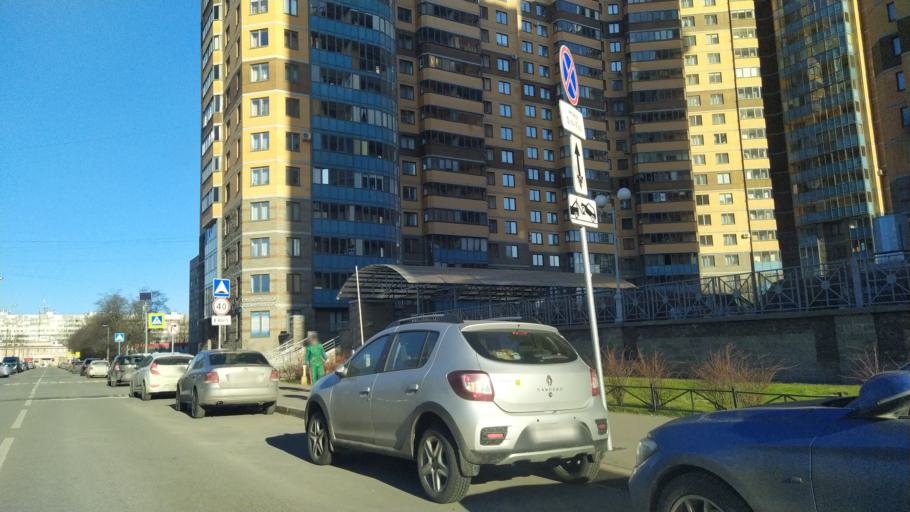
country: RU
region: St.-Petersburg
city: Grazhdanka
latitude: 60.0401
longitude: 30.4073
